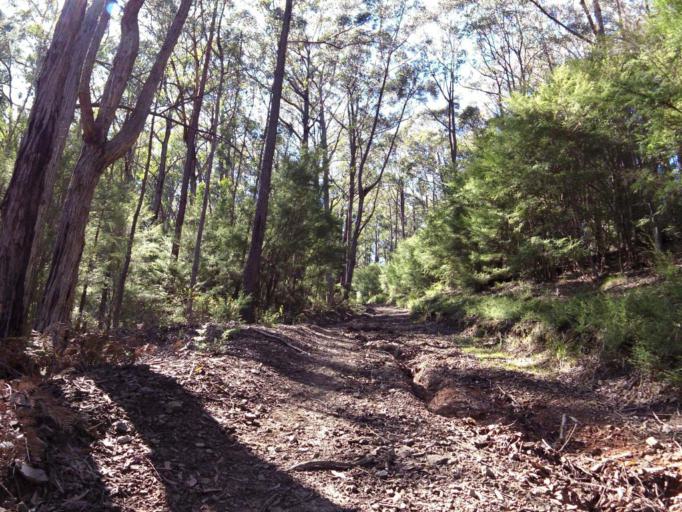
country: AU
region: Victoria
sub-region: Yarra Ranges
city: Launching Place
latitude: -37.7431
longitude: 145.5584
